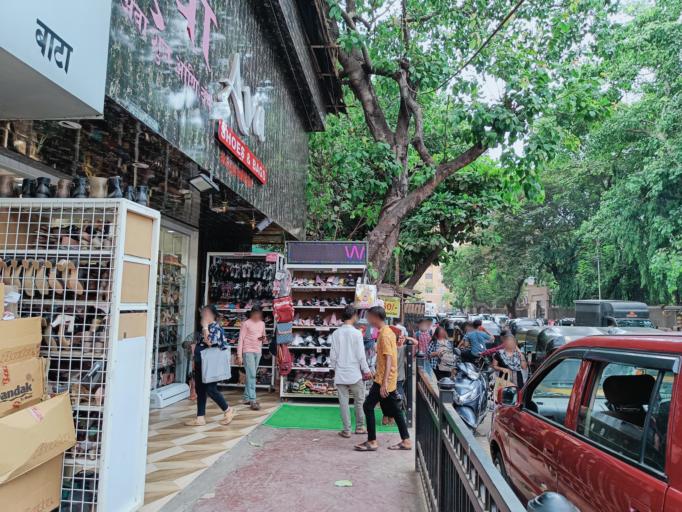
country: IN
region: Maharashtra
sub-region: Mumbai Suburban
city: Mumbai
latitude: 19.1082
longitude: 72.8385
